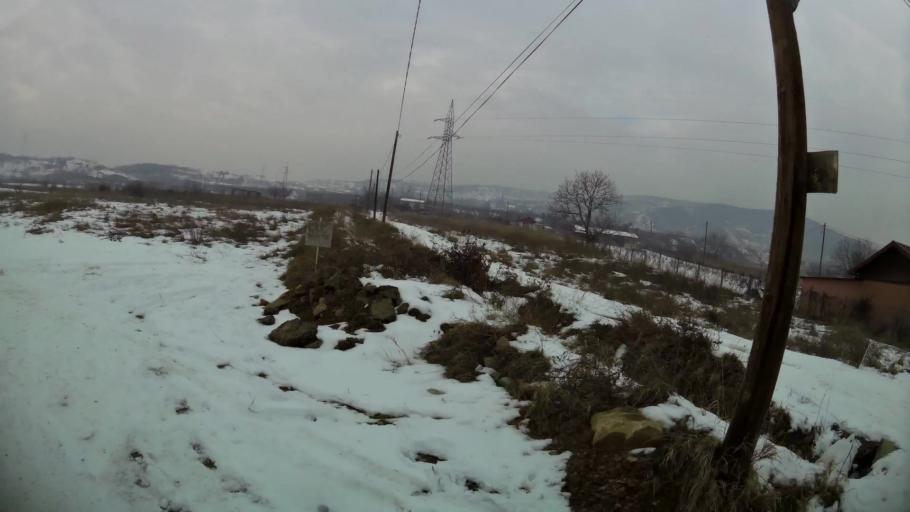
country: MK
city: Kondovo
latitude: 42.0381
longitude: 21.3393
